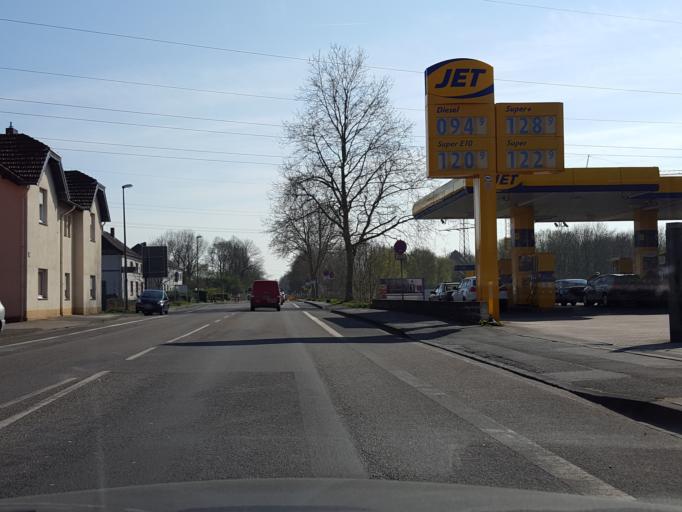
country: DE
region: North Rhine-Westphalia
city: Castrop-Rauxel
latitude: 51.5981
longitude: 7.3122
